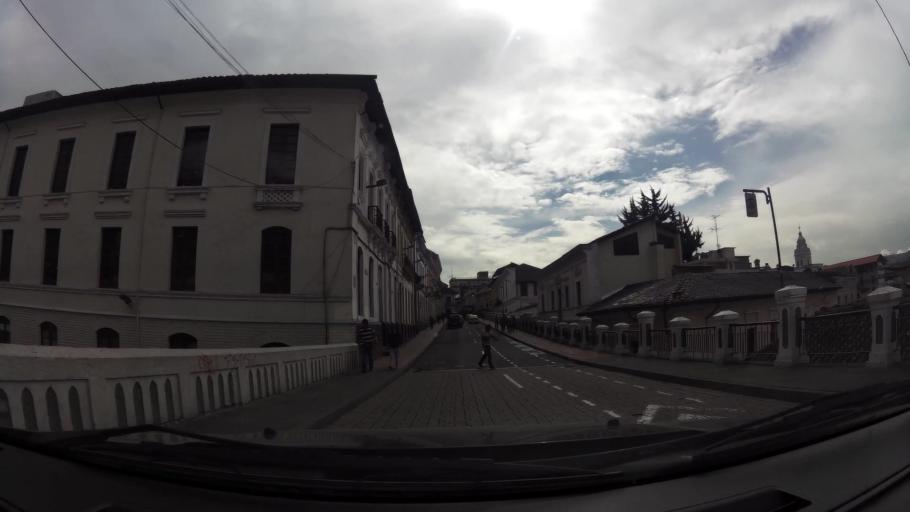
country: EC
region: Pichincha
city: Quito
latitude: -0.2240
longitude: -78.5149
